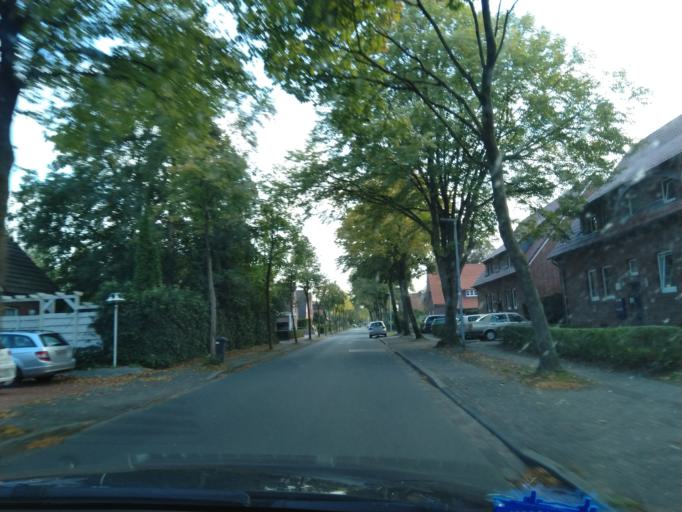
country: DE
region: Lower Saxony
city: Papenburg
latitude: 53.0714
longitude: 7.4092
